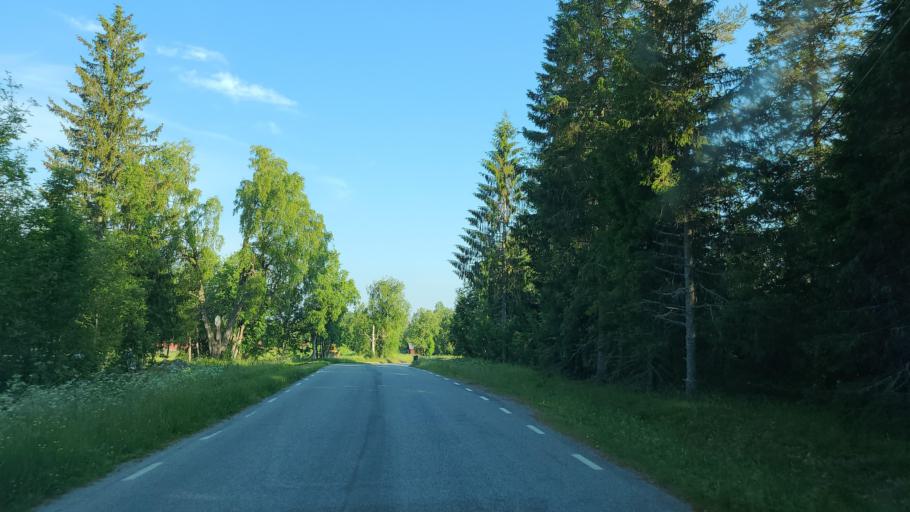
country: SE
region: Vaesterbotten
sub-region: Skelleftea Kommun
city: Burea
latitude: 64.3498
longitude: 21.3363
